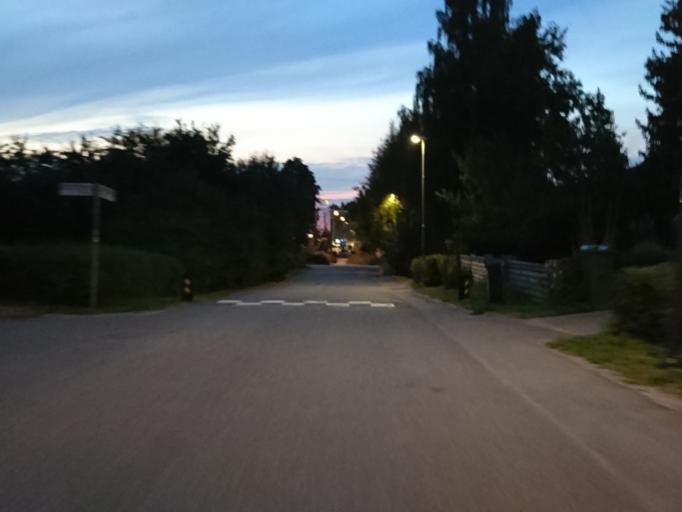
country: SE
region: Stockholm
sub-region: Huddinge Kommun
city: Segeltorp
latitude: 59.2810
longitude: 17.9362
